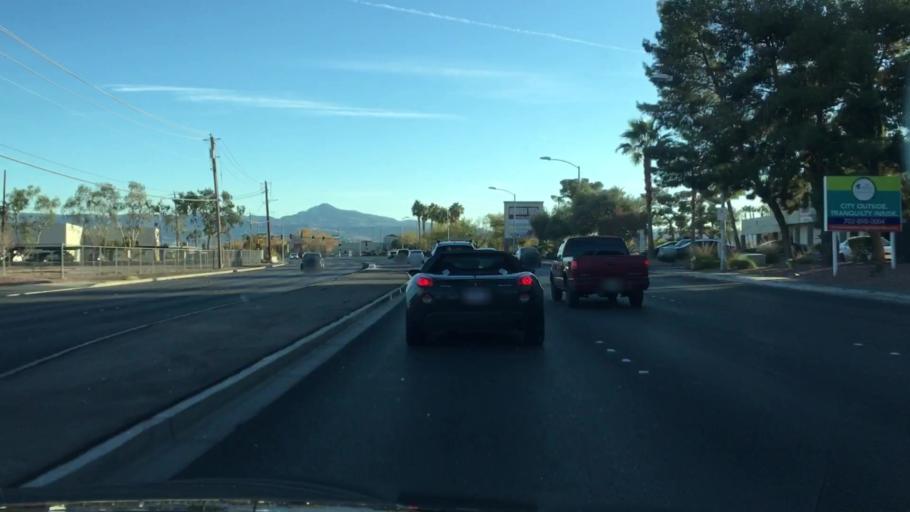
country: US
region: Nevada
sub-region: Clark County
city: Whitney
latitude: 36.0758
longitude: -115.0733
